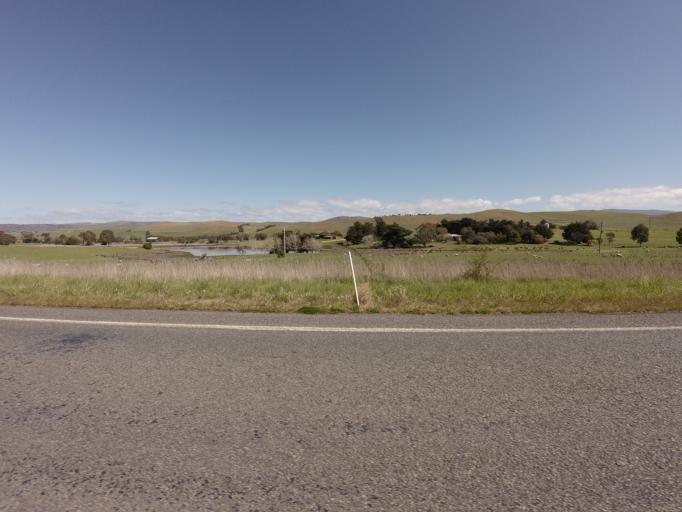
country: AU
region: Tasmania
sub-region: Derwent Valley
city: New Norfolk
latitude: -42.5497
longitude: 146.7892
